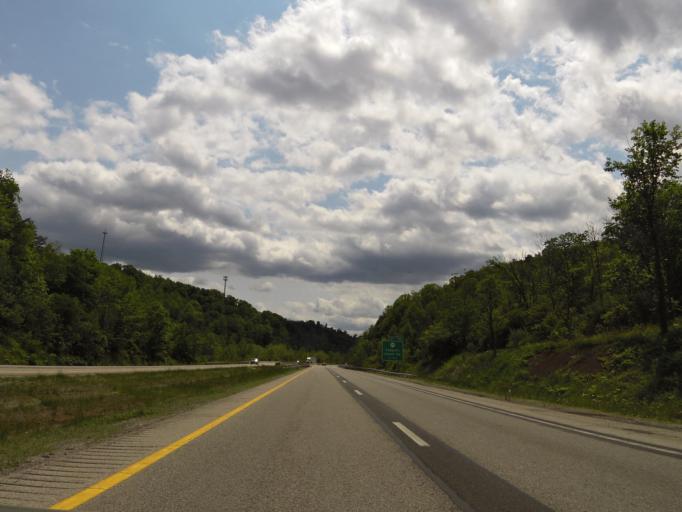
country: US
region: West Virginia
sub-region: Kanawha County
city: Sissonville
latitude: 38.4732
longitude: -81.6439
